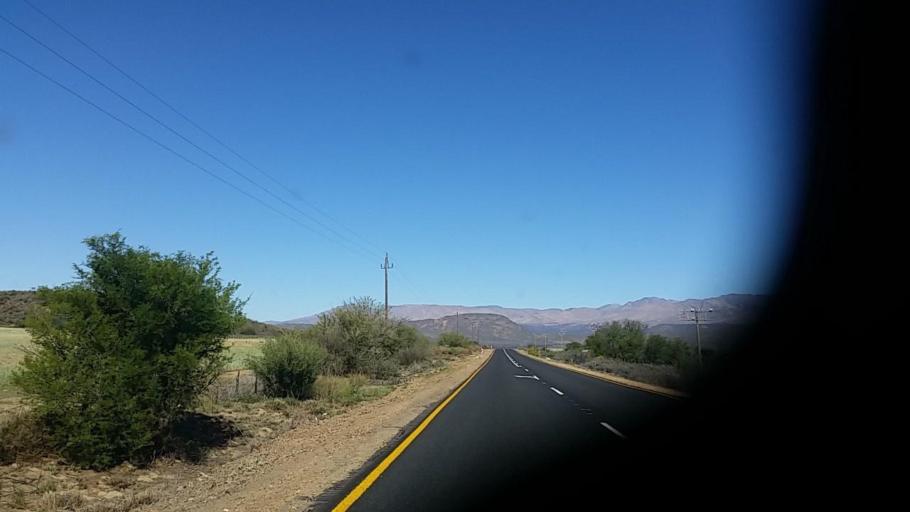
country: ZA
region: Western Cape
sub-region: Eden District Municipality
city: Oudtshoorn
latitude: -33.4834
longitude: 22.6599
